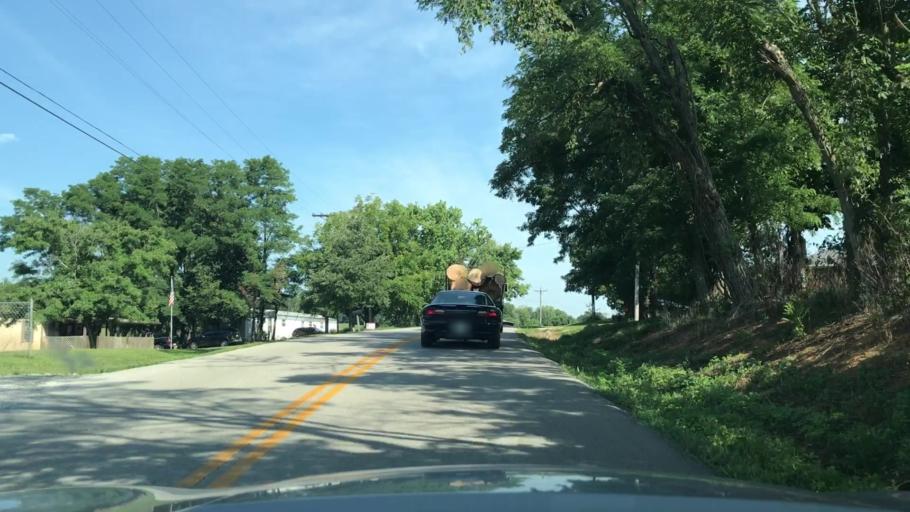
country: US
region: Kentucky
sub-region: Clinton County
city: Albany
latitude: 36.7533
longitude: -84.9952
